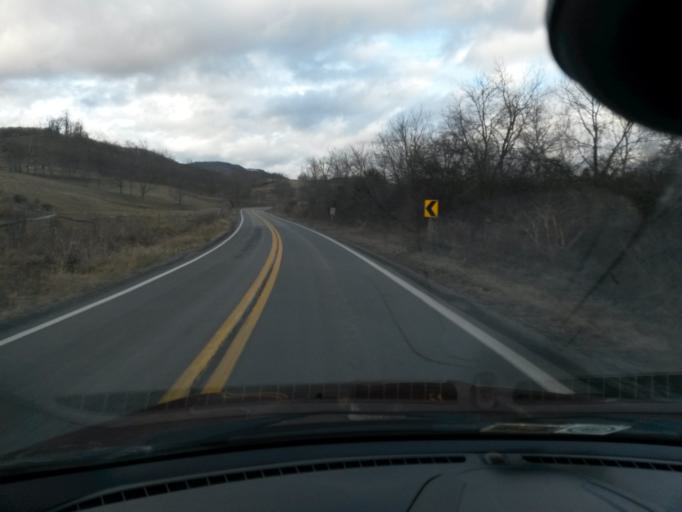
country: US
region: West Virginia
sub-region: Monroe County
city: Union
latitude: 37.5824
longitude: -80.5492
